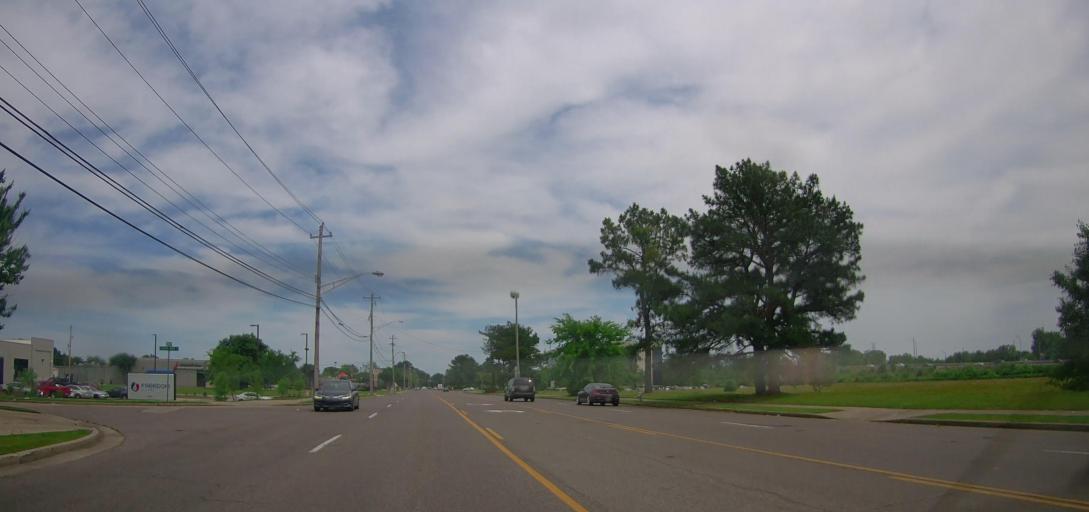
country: US
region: Tennessee
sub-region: Shelby County
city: Germantown
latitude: 35.0707
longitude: -89.8474
